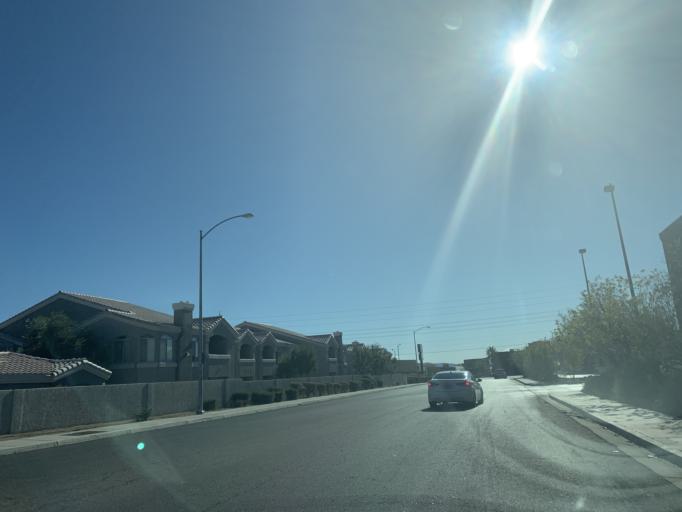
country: US
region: Nevada
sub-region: Clark County
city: Summerlin South
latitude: 36.1162
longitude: -115.2937
